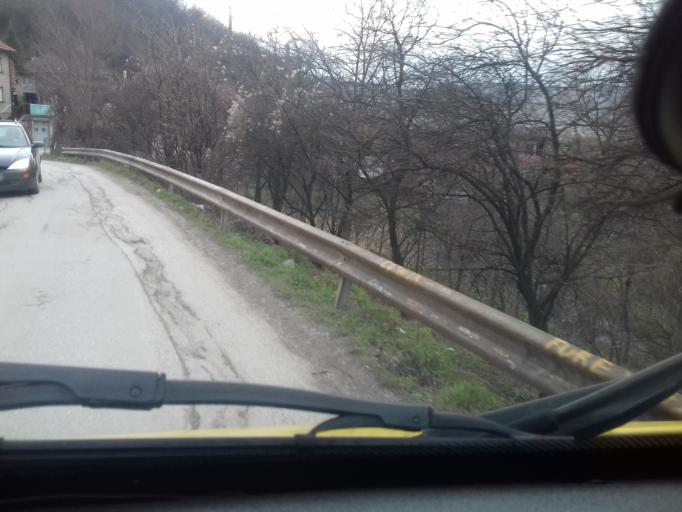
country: BA
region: Federation of Bosnia and Herzegovina
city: Zenica
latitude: 44.2329
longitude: 17.9098
